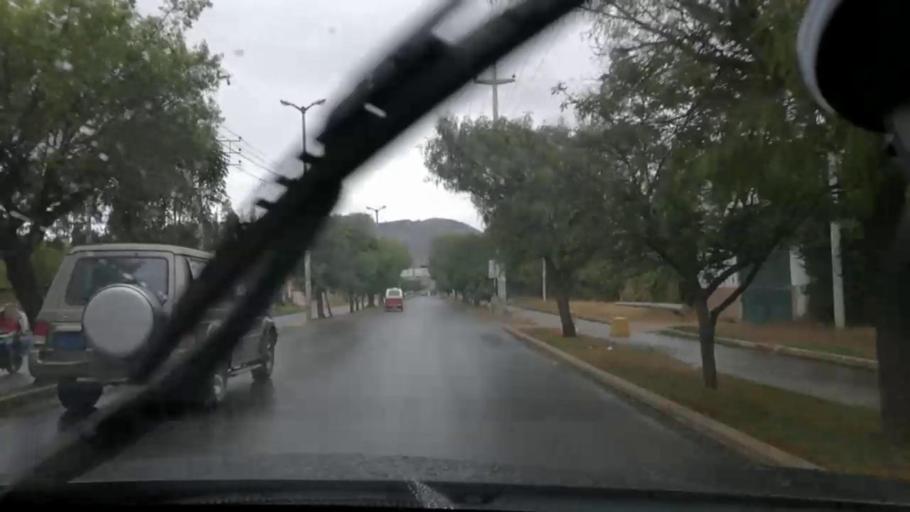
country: PE
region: Cajamarca
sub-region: Provincia de Cajamarca
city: Cajamarca
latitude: -7.1652
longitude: -78.4799
